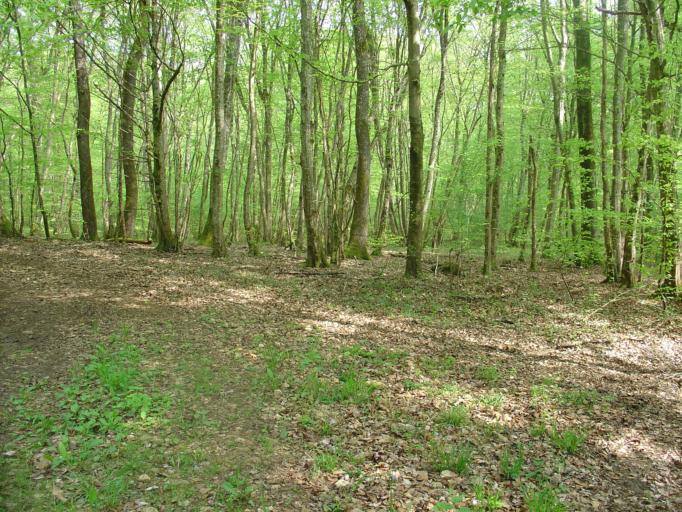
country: FR
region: Lorraine
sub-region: Departement de Meurthe-et-Moselle
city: Montauville
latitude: 48.8361
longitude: 5.9479
